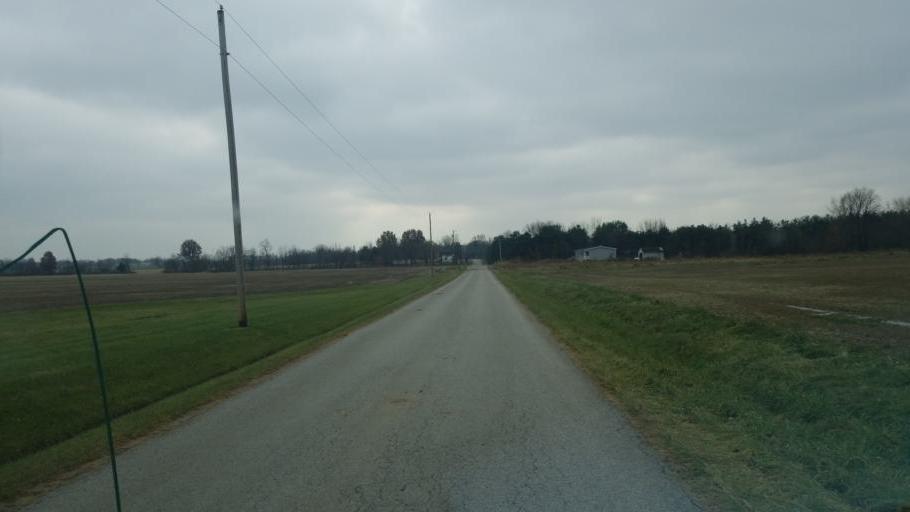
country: US
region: Ohio
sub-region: Morrow County
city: Cardington
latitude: 40.4277
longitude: -82.8344
